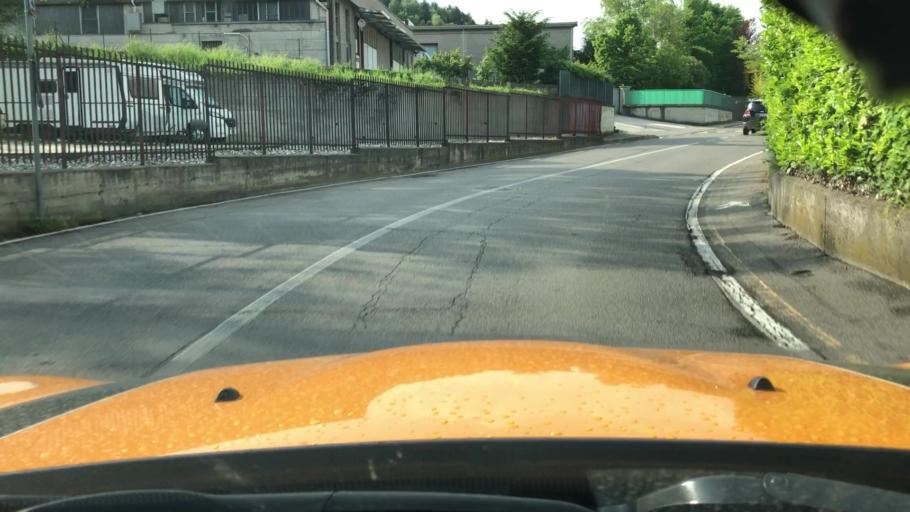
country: IT
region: Lombardy
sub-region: Provincia di Como
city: Senna Comasco
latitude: 45.7620
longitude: 9.1134
